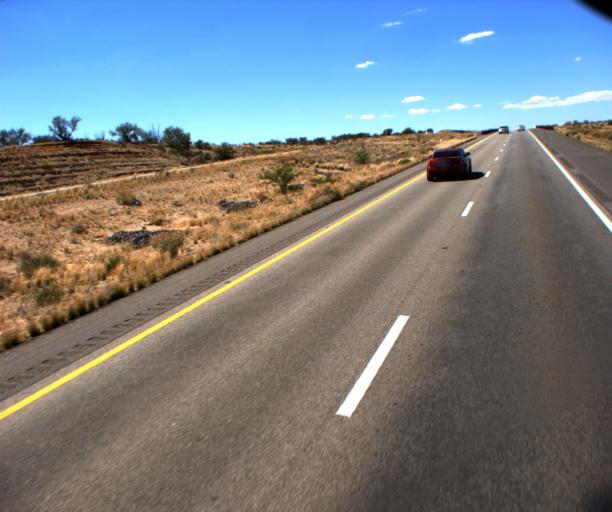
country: US
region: Arizona
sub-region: Mohave County
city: Kingman
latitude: 34.8596
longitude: -113.6407
